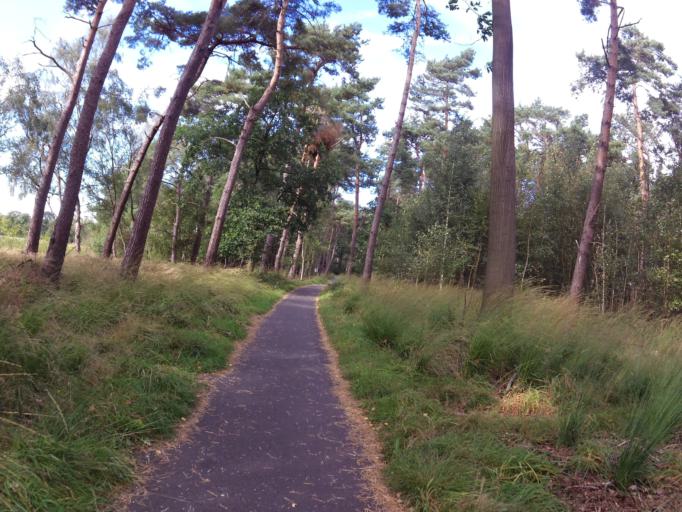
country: NL
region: North Brabant
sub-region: Gemeente Valkenswaard
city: Valkenswaard
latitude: 51.3522
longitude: 5.5152
